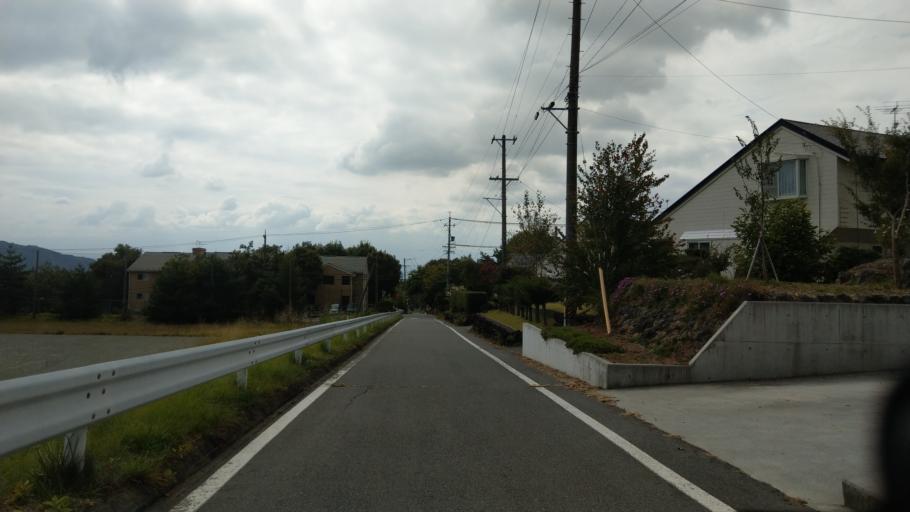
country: JP
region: Nagano
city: Komoro
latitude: 36.3230
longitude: 138.5263
